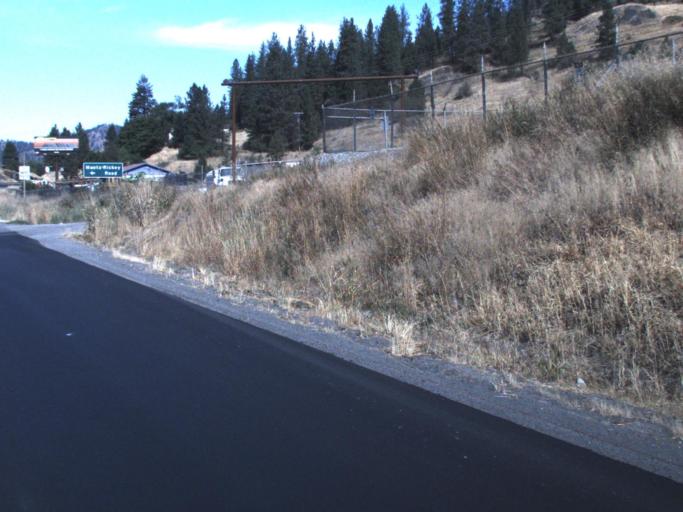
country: US
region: Washington
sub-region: Stevens County
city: Colville
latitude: 48.5186
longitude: -117.9014
